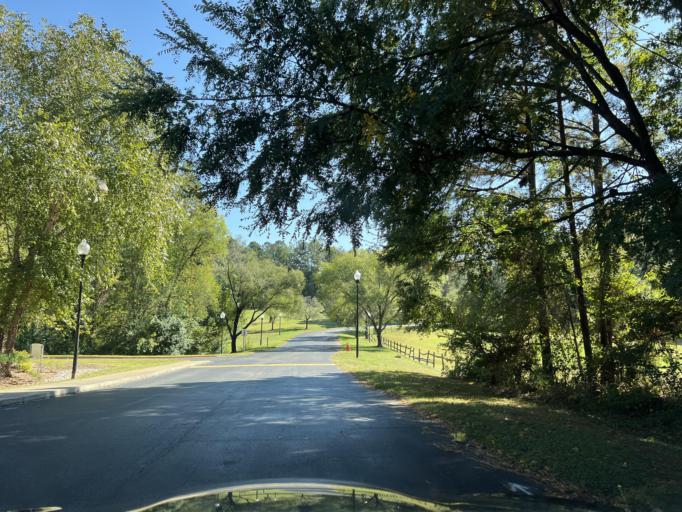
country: US
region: North Carolina
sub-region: Wake County
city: Raleigh
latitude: 35.7409
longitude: -78.6622
